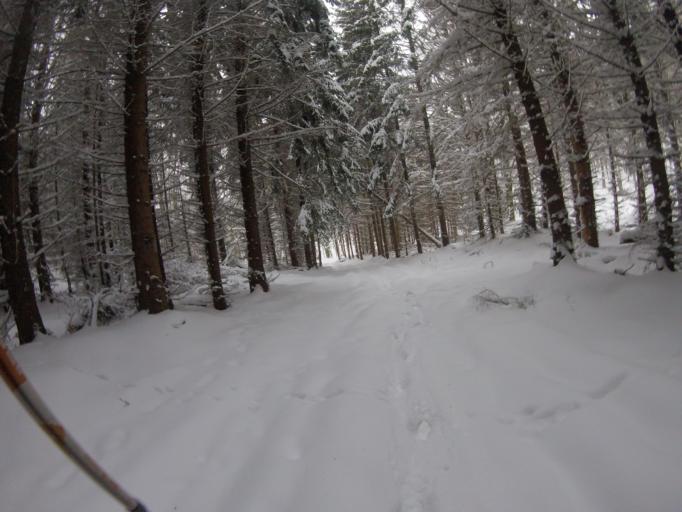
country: HU
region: Heves
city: Szilvasvarad
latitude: 48.0598
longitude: 20.4265
